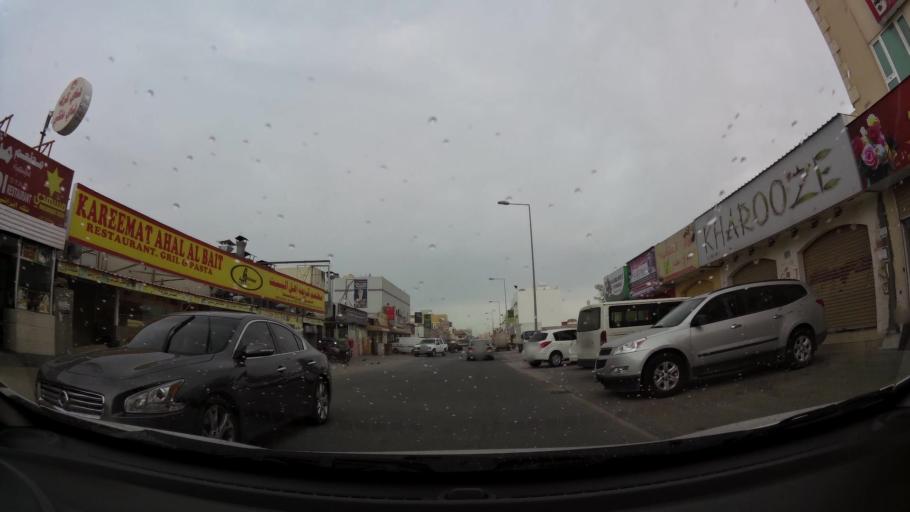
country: BH
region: Central Governorate
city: Madinat Hamad
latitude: 26.0946
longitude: 50.4869
